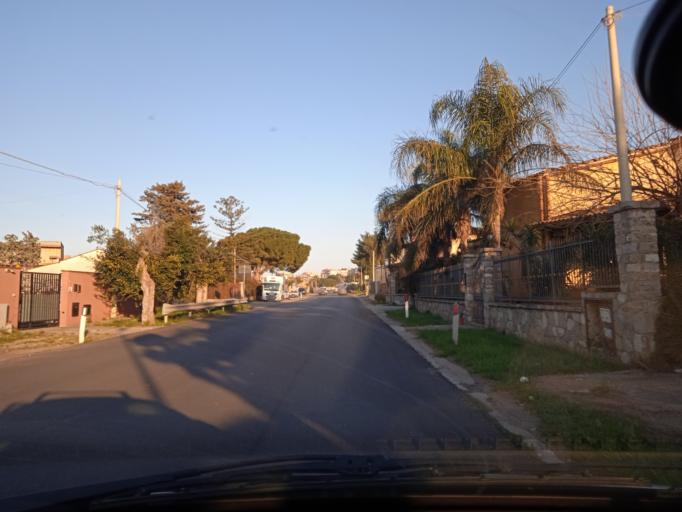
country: IT
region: Sicily
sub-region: Palermo
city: Bagheria
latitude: 38.0895
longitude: 13.4915
